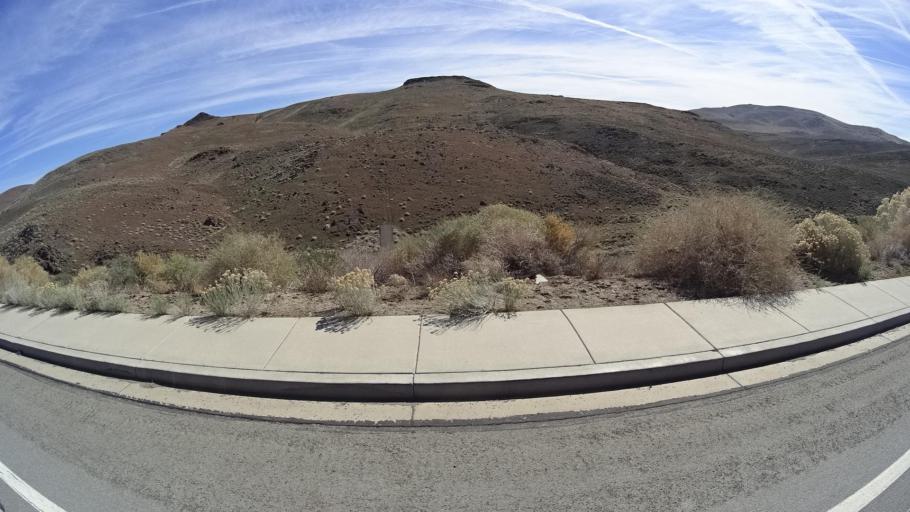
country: US
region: Nevada
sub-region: Washoe County
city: Spanish Springs
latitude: 39.5780
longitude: -119.6881
